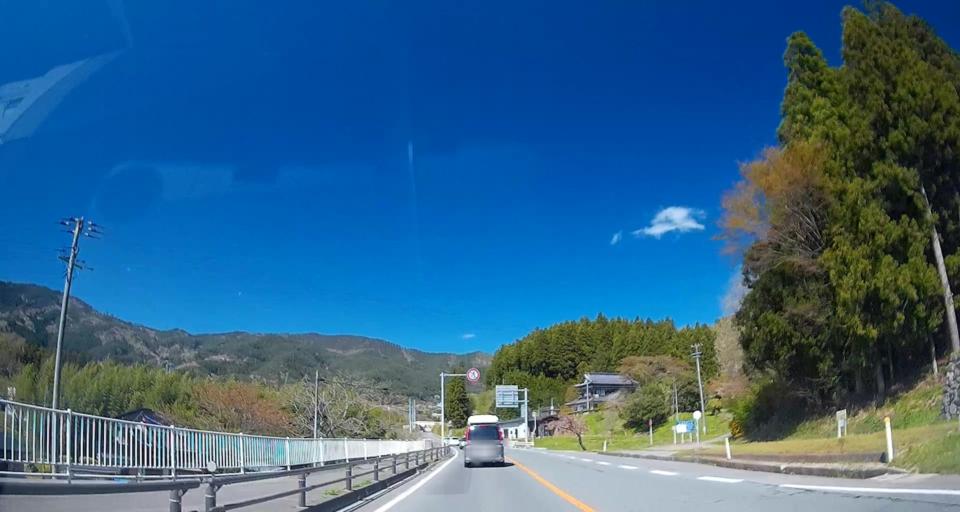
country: JP
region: Iwate
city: Ofunato
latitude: 39.0167
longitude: 141.6692
